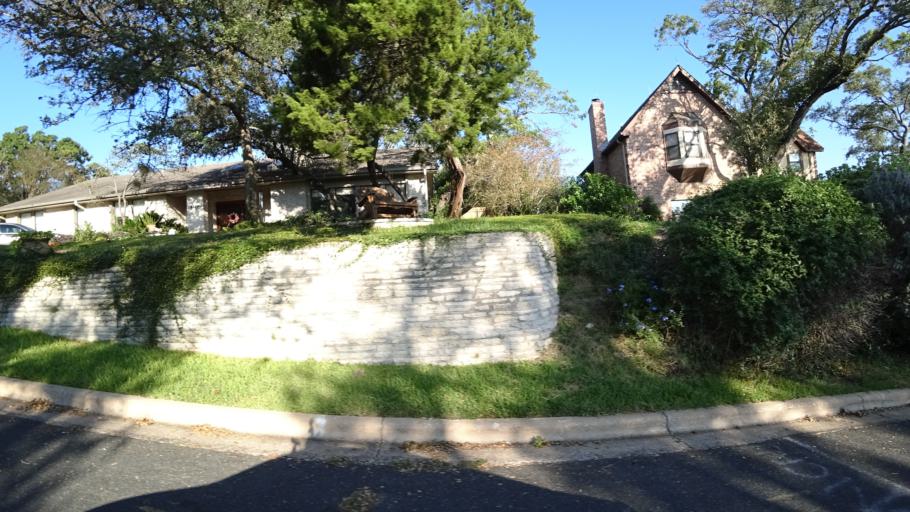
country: US
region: Texas
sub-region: Travis County
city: Rollingwood
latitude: 30.2625
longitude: -97.8065
